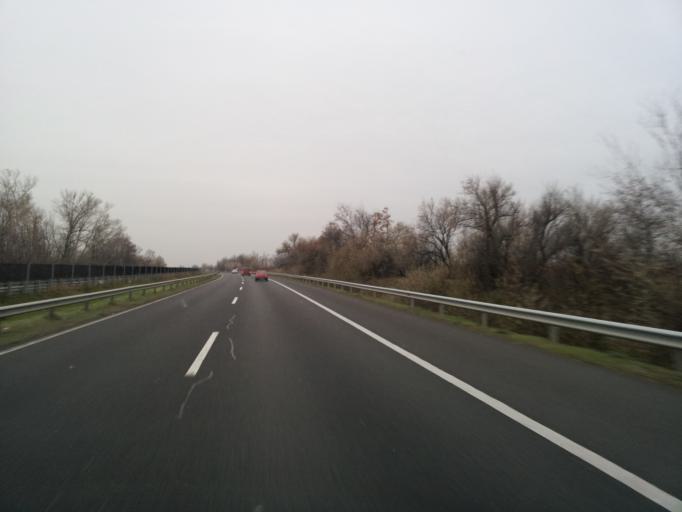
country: HU
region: Fejer
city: Baracska
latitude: 47.2859
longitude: 18.7165
